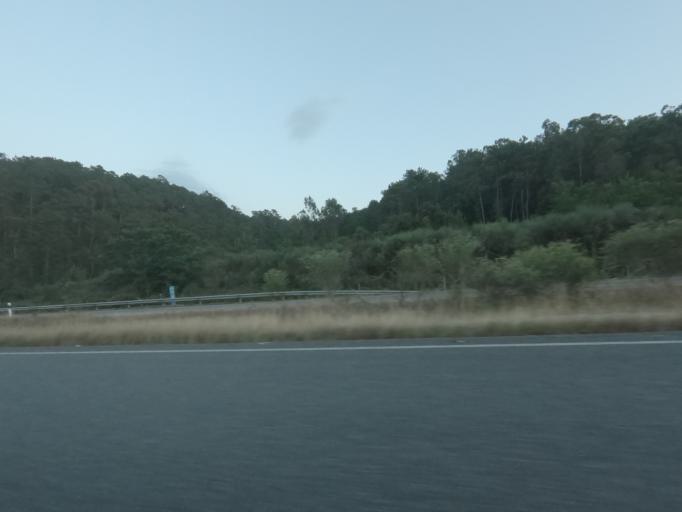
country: ES
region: Galicia
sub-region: Provincia de Pontevedra
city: Porrino
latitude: 42.1773
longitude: -8.5626
